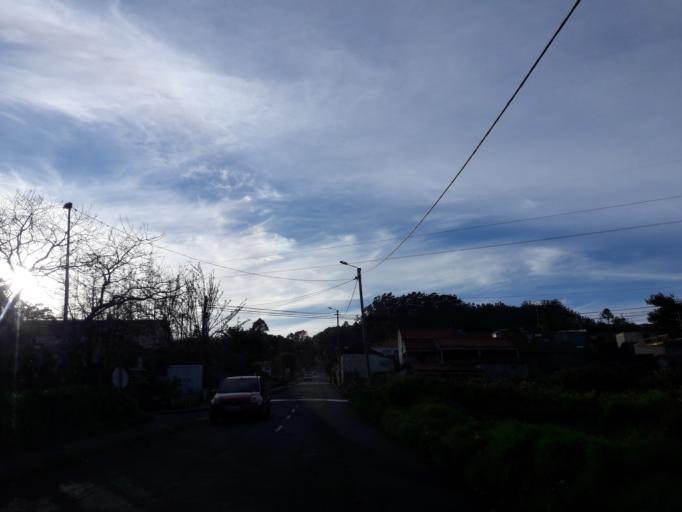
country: PT
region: Madeira
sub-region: Santa Cruz
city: Camacha
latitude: 32.6708
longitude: -16.8463
